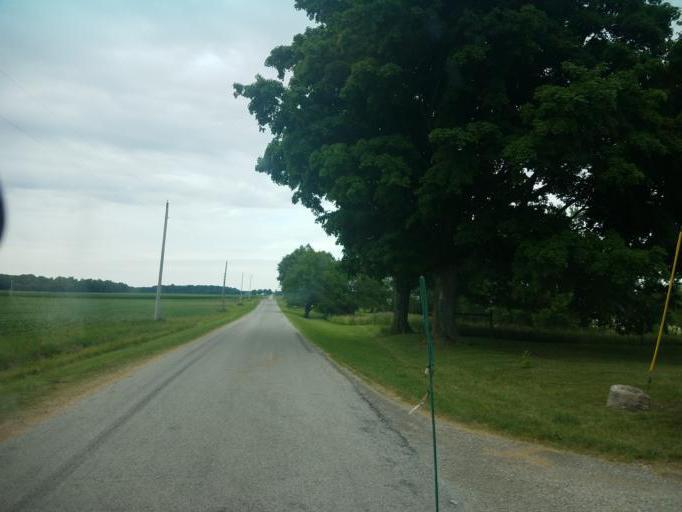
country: US
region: Ohio
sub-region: Union County
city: Richwood
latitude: 40.6197
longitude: -83.3429
